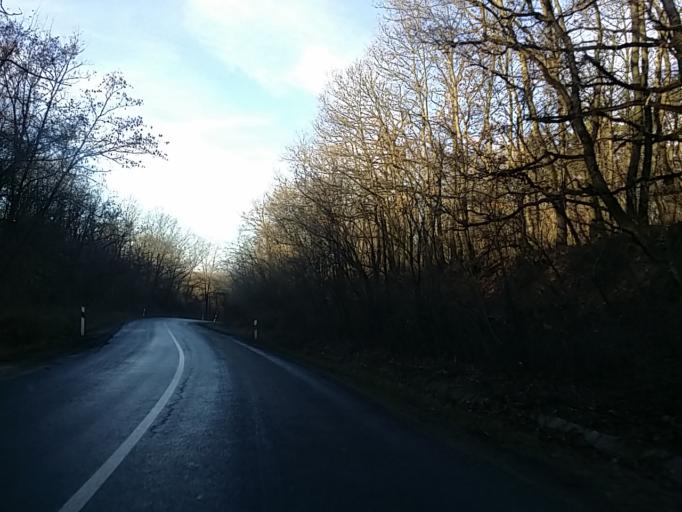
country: HU
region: Pest
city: Telki
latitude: 47.5370
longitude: 18.8517
